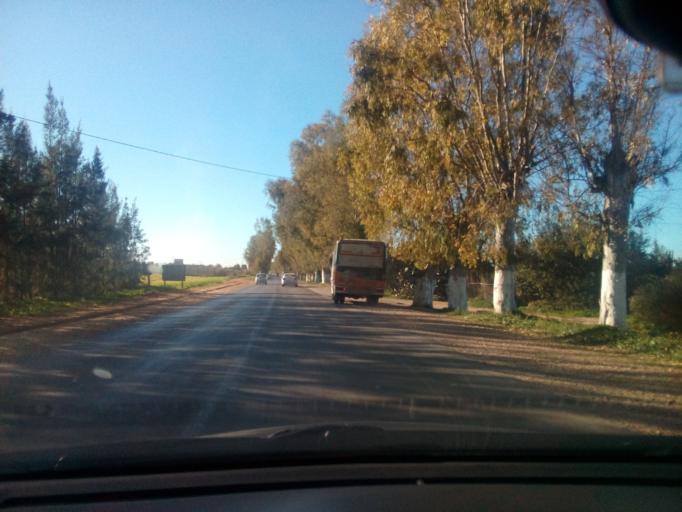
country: DZ
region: Mostaganem
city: Mostaganem
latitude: 35.9041
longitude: 0.2088
